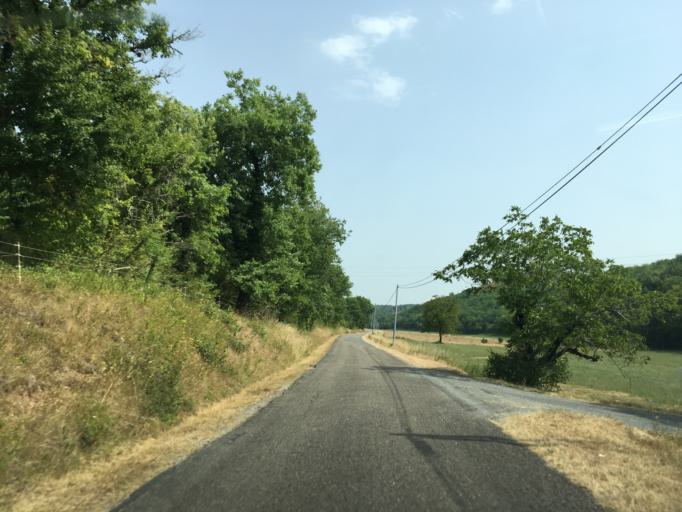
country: FR
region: Midi-Pyrenees
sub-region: Departement du Lot
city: Le Vigan
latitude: 44.7480
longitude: 1.5262
